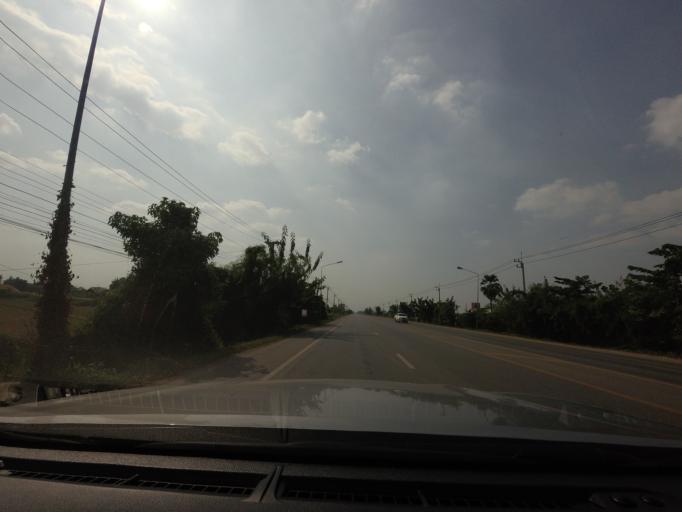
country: TH
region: Phitsanulok
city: Bang Rakam
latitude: 16.7724
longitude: 100.1677
